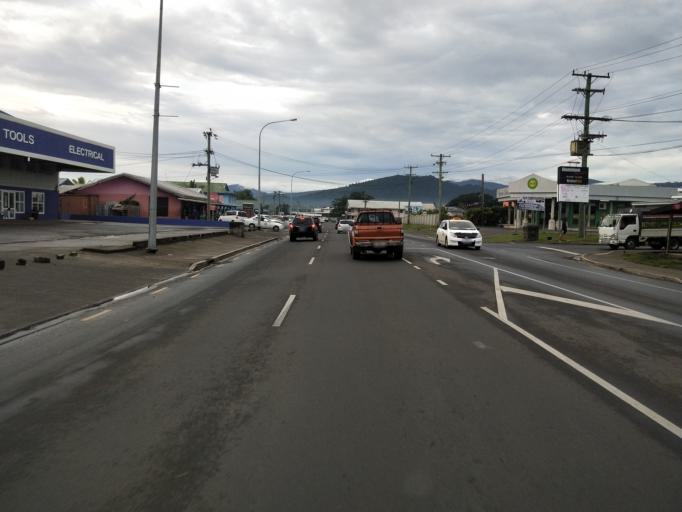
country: WS
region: Tuamasaga
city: Vaiusu
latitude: -13.8183
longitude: -171.8067
